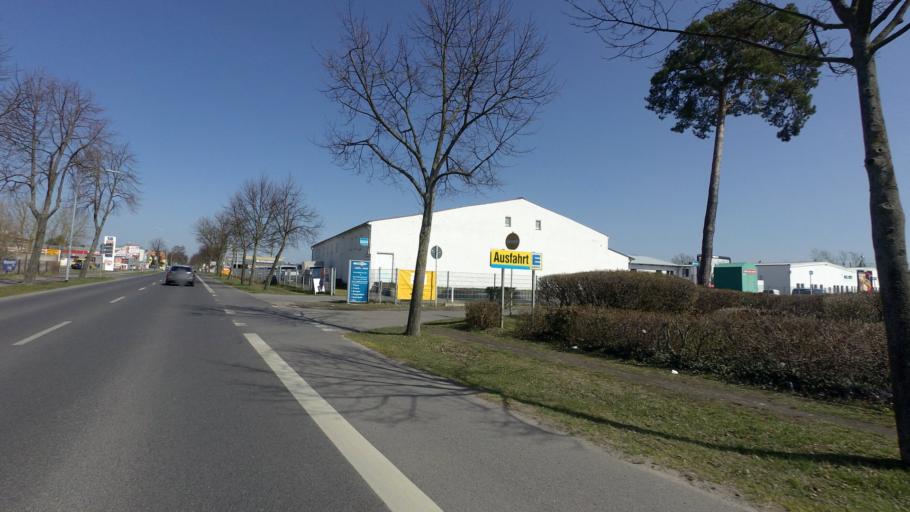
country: DE
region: Brandenburg
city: Oranienburg
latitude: 52.7643
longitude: 13.2452
